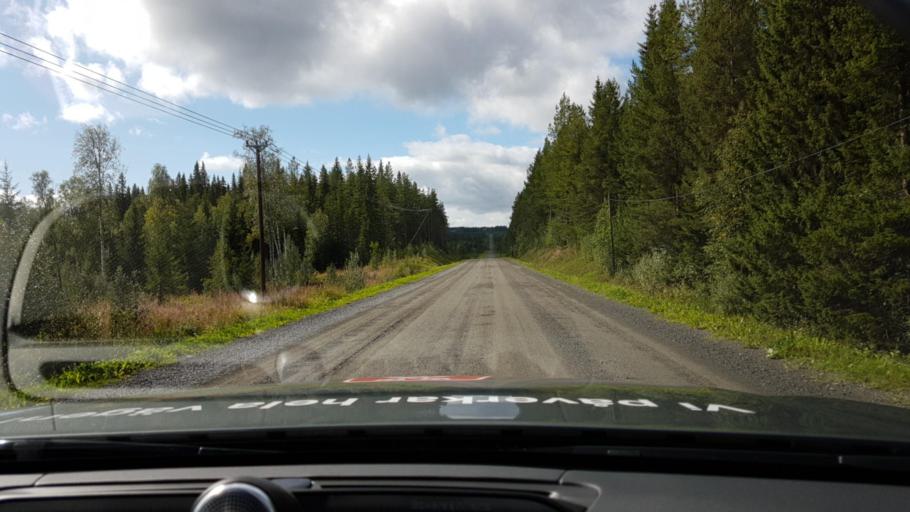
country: SE
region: Jaemtland
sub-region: OEstersunds Kommun
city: Lit
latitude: 63.6228
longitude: 15.1549
